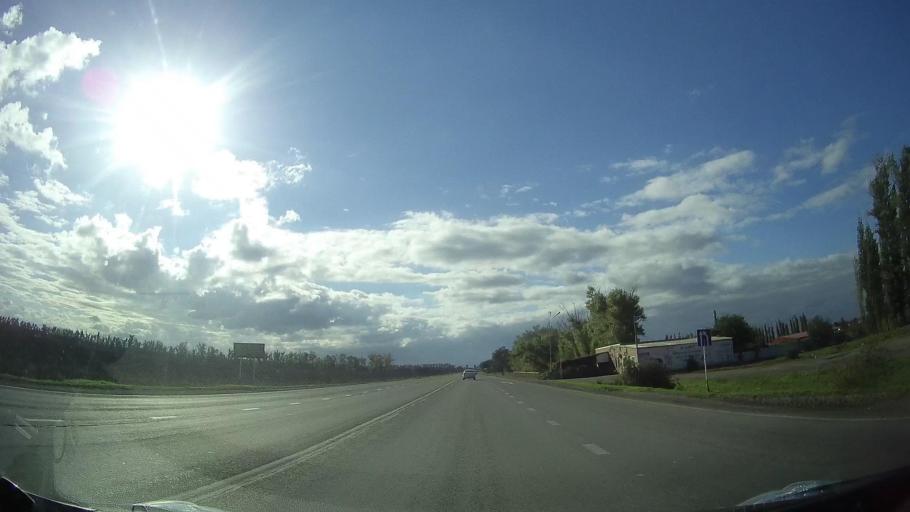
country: RU
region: Rostov
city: Tselina
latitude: 46.5327
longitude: 40.9770
